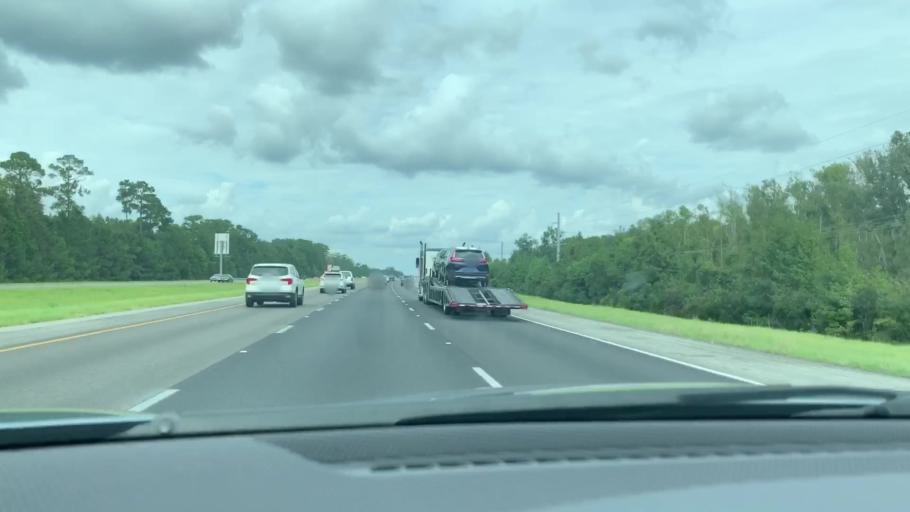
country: US
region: Georgia
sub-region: Liberty County
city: Midway
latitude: 31.7943
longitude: -81.3736
